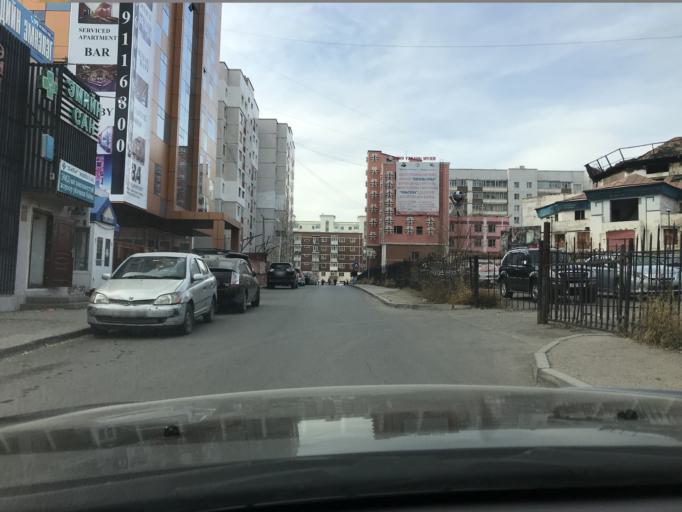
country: MN
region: Ulaanbaatar
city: Ulaanbaatar
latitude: 47.9175
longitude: 106.9433
